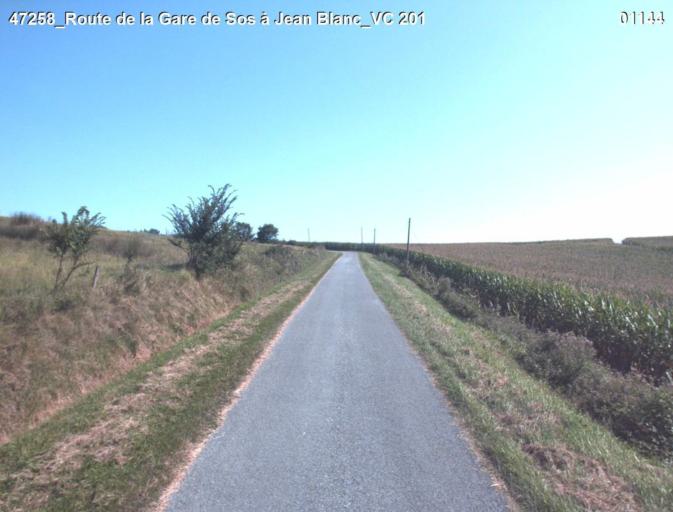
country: FR
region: Midi-Pyrenees
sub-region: Departement du Gers
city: Montreal
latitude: 44.0337
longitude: 0.1498
